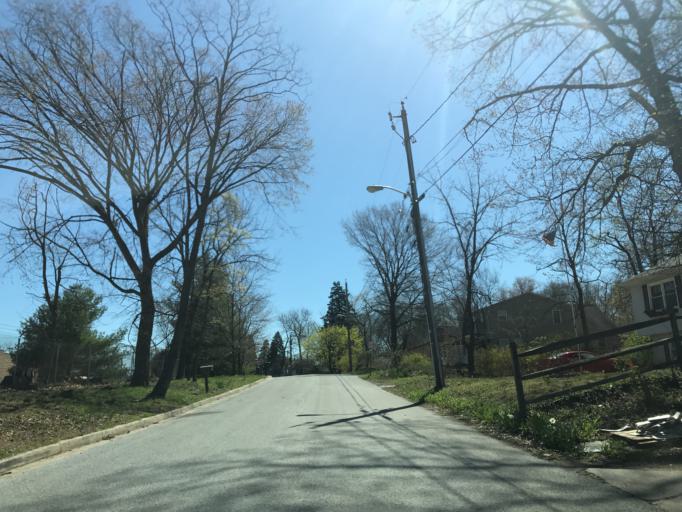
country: US
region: Maryland
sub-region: Anne Arundel County
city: Odenton
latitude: 39.0877
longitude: -76.7111
